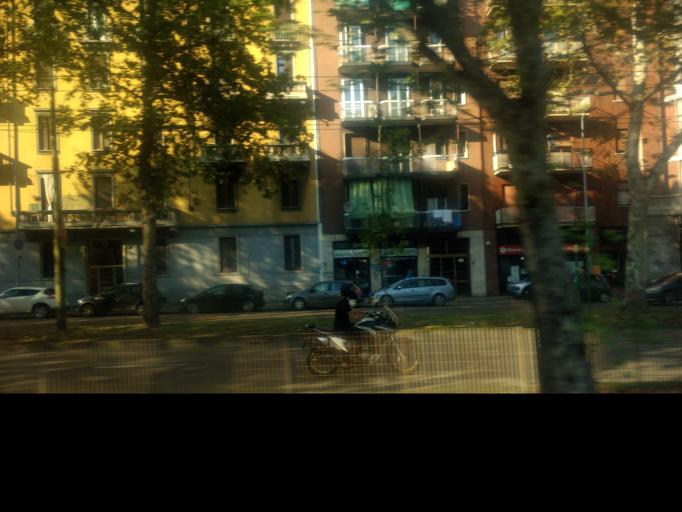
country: IT
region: Lombardy
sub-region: Citta metropolitana di Milano
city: Milano
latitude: 45.4970
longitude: 9.1696
